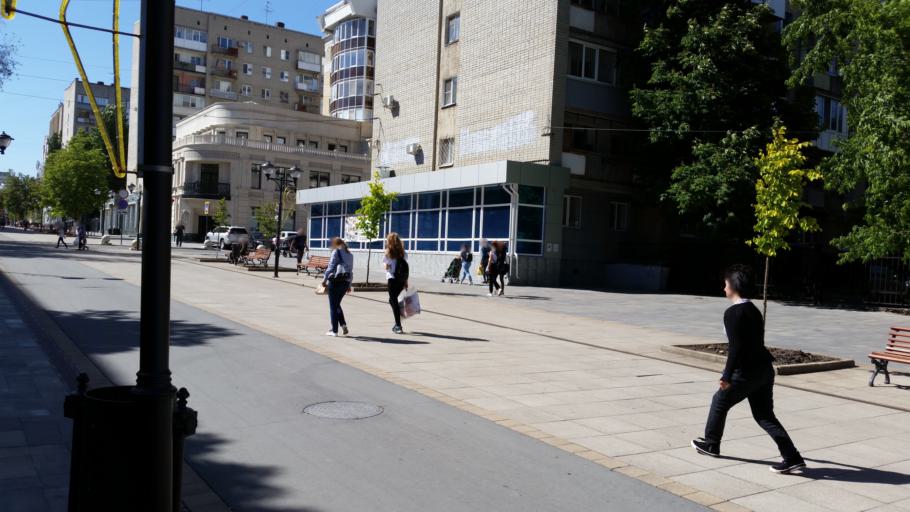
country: RU
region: Saratov
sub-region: Saratovskiy Rayon
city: Saratov
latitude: 51.5284
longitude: 46.0432
